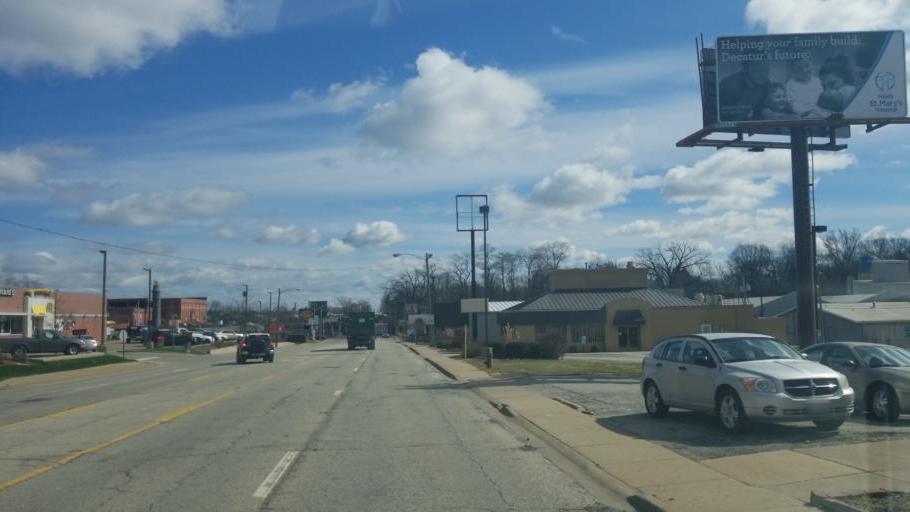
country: US
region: Illinois
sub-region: Macon County
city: Decatur
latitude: 39.8455
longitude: -88.9709
